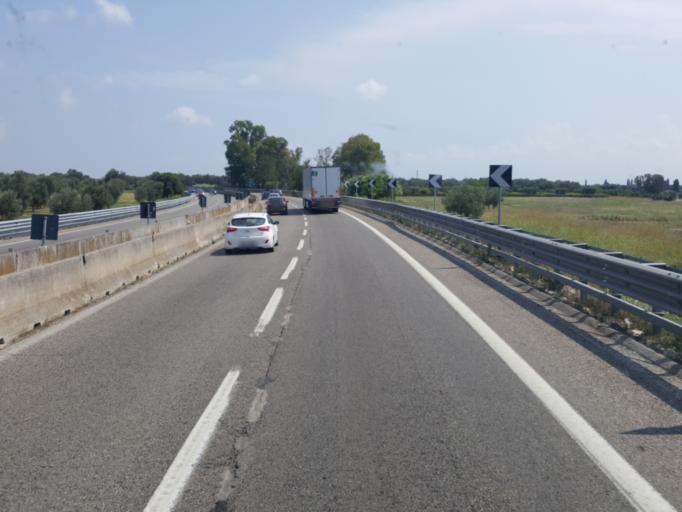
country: IT
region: Apulia
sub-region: Provincia di Brindisi
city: San Pietro Vernotico
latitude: 40.5054
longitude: 18.0247
